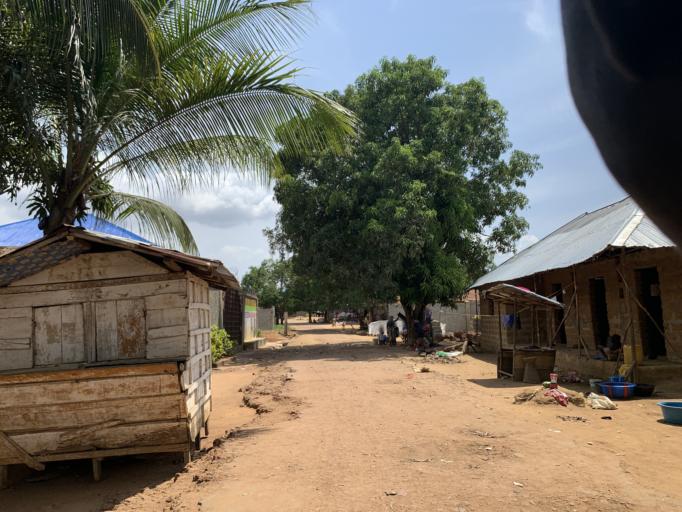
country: SL
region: Western Area
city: Waterloo
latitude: 8.3365
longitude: -13.0371
